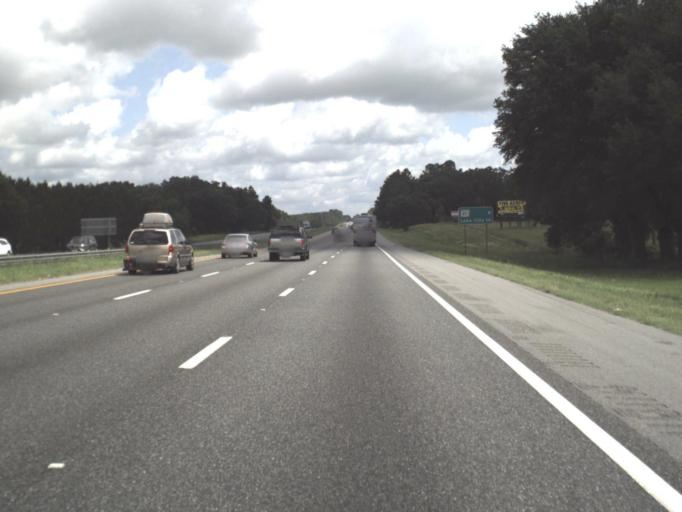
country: US
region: Florida
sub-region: Columbia County
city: Watertown
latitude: 30.0101
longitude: -82.6054
